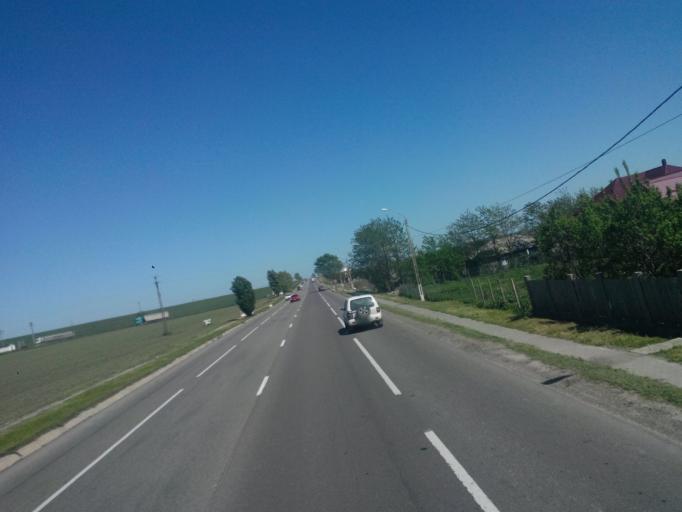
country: RO
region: Iasi
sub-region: Comuna Ion Neculce
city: Razboieni
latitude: 47.2198
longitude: 27.0660
